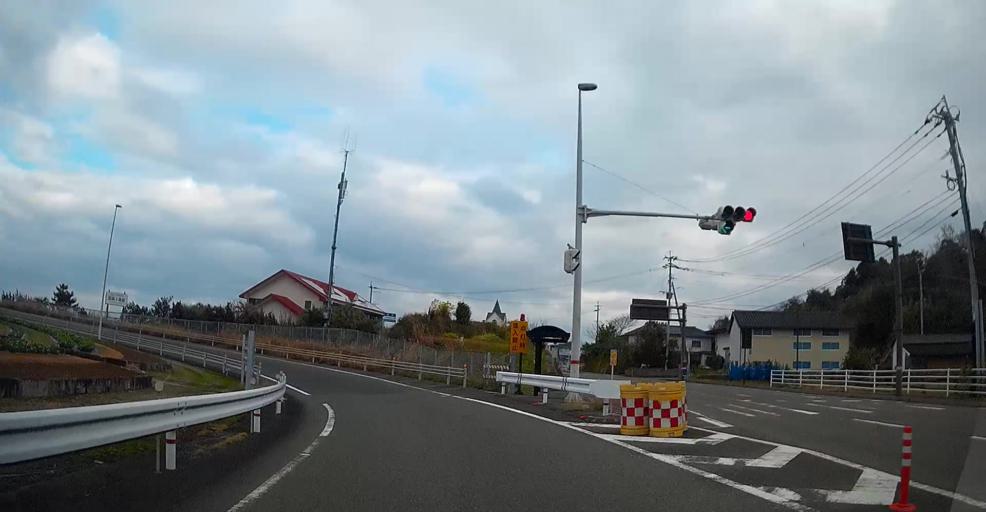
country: JP
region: Kumamoto
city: Hondo
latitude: 32.5049
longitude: 130.3033
